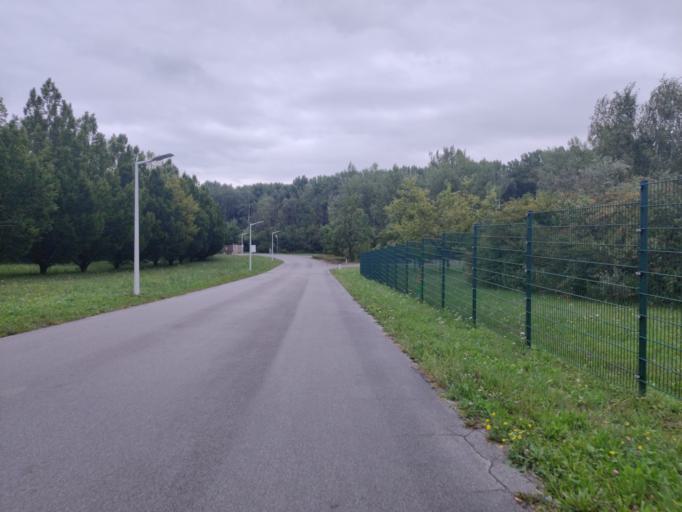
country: AT
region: Lower Austria
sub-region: Politischer Bezirk Korneuburg
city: Spillern
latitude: 48.3577
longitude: 16.2418
